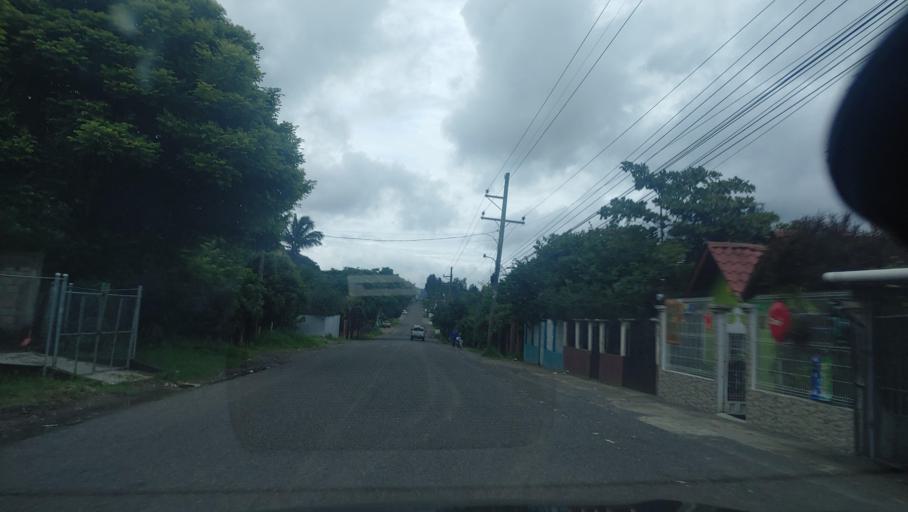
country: HN
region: Choluteca
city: San Marcos de Colon
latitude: 13.3757
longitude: -86.9013
